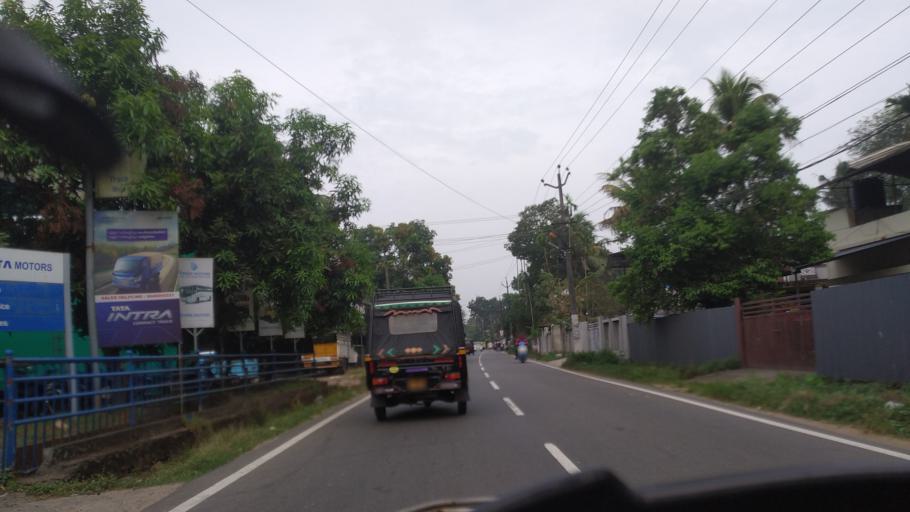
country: IN
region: Kerala
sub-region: Thrissur District
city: Kodungallur
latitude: 10.1483
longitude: 76.2468
